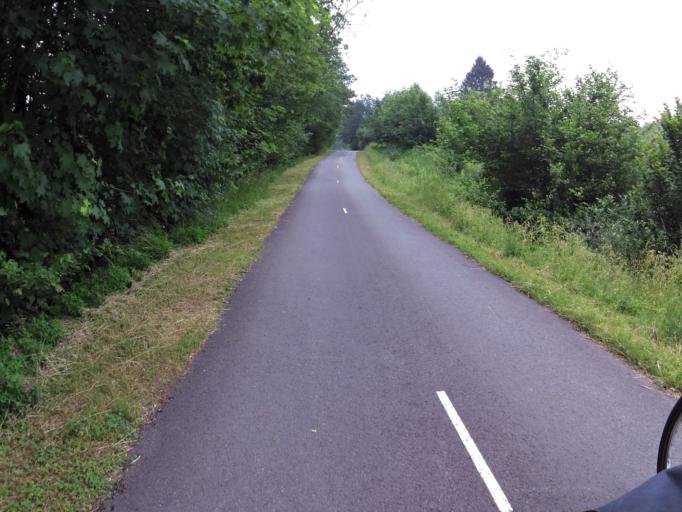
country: FR
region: Champagne-Ardenne
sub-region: Departement des Ardennes
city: Fumay
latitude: 49.9790
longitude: 4.6743
